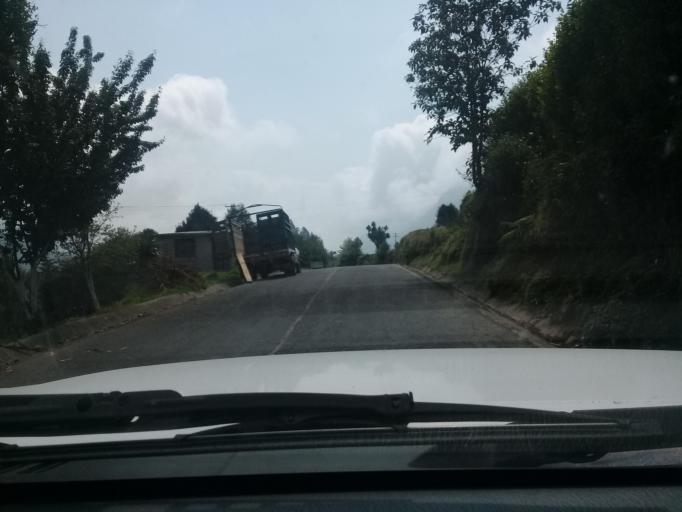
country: MX
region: Veracruz
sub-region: Mariano Escobedo
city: San Isidro el Berro
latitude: 18.9465
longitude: -97.2198
